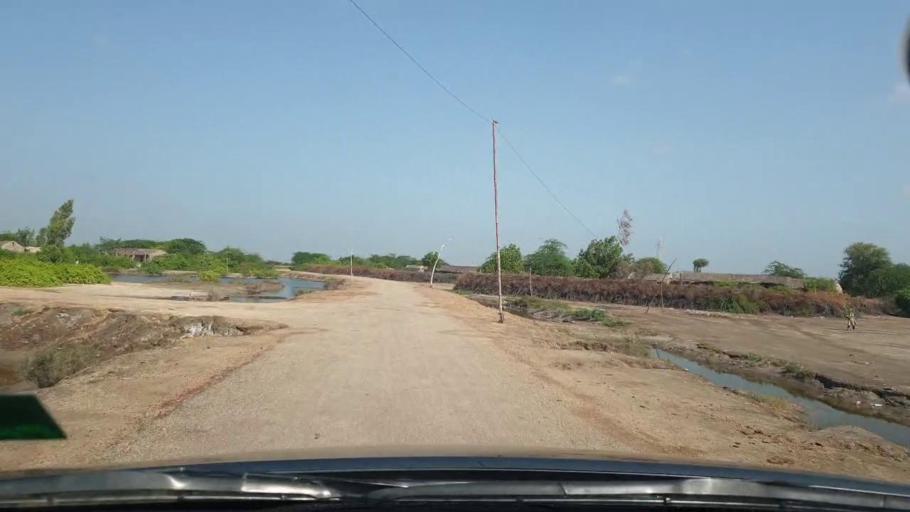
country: PK
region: Sindh
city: Tando Bago
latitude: 24.7471
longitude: 68.9783
